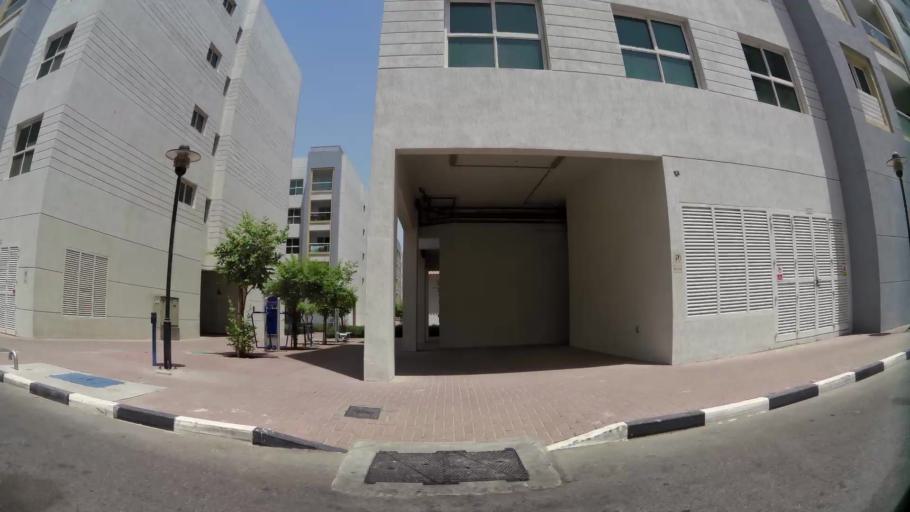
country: AE
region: Ash Shariqah
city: Sharjah
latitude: 25.2760
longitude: 55.4184
